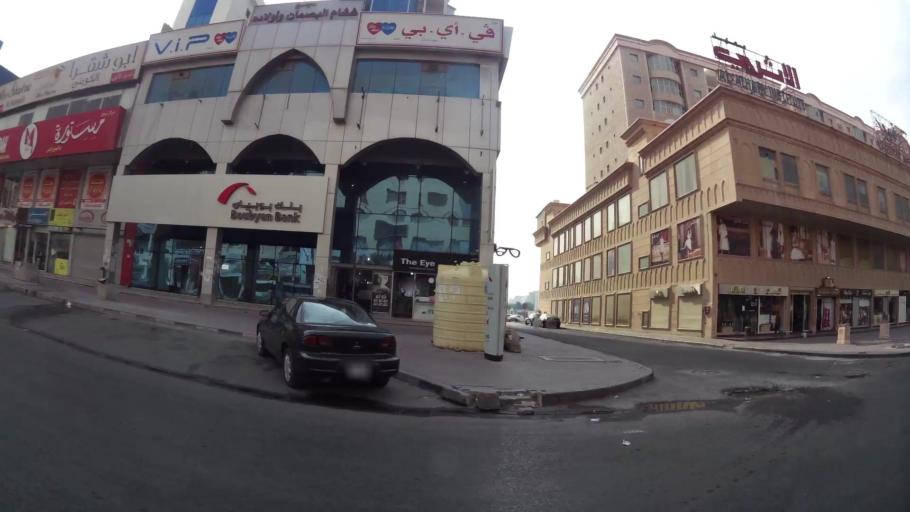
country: KW
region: Al Farwaniyah
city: Al Farwaniyah
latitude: 29.2743
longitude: 47.9640
